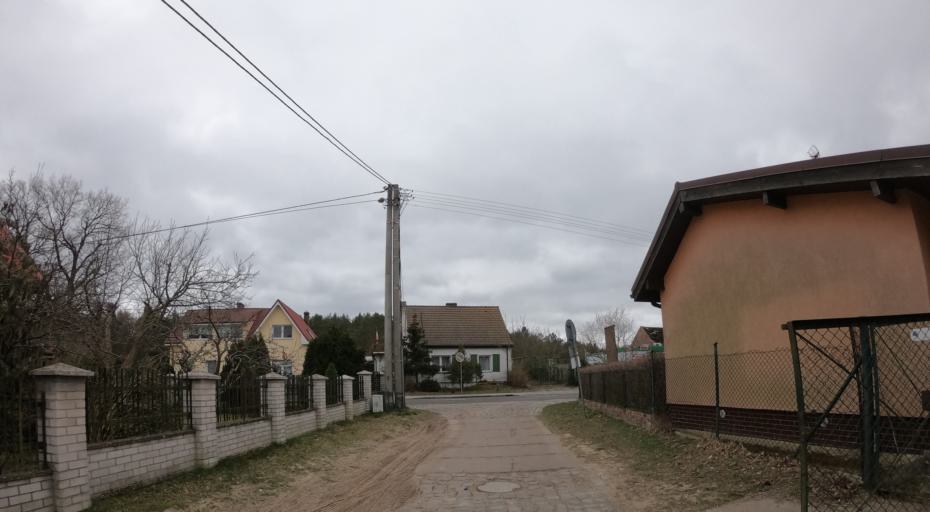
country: PL
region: West Pomeranian Voivodeship
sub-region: Powiat policki
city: Nowe Warpno
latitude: 53.6752
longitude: 14.3816
